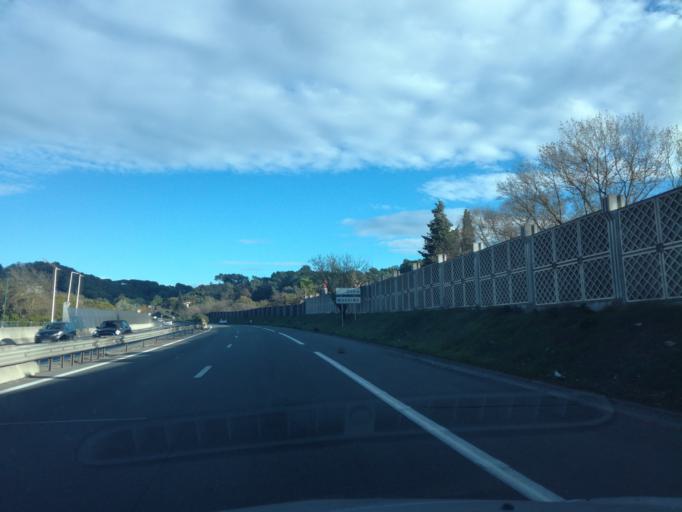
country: FR
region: Provence-Alpes-Cote d'Azur
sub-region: Departement des Alpes-Maritimes
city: Mouans-Sartoux
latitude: 43.6080
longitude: 6.9767
